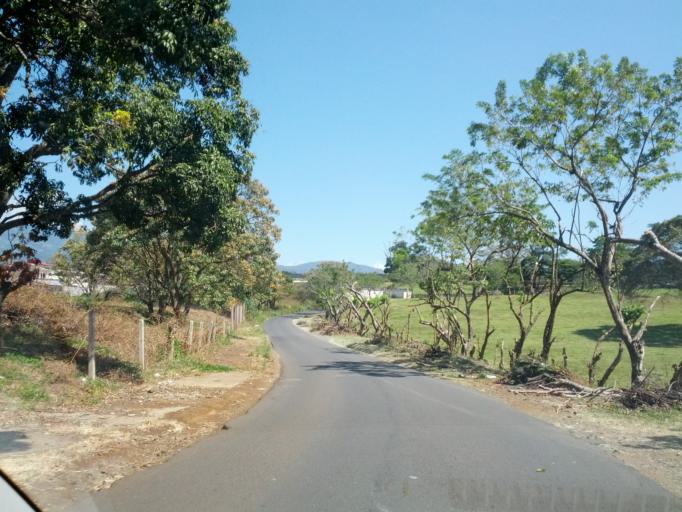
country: CR
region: Alajuela
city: Alajuela
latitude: 10.0090
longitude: -84.1935
